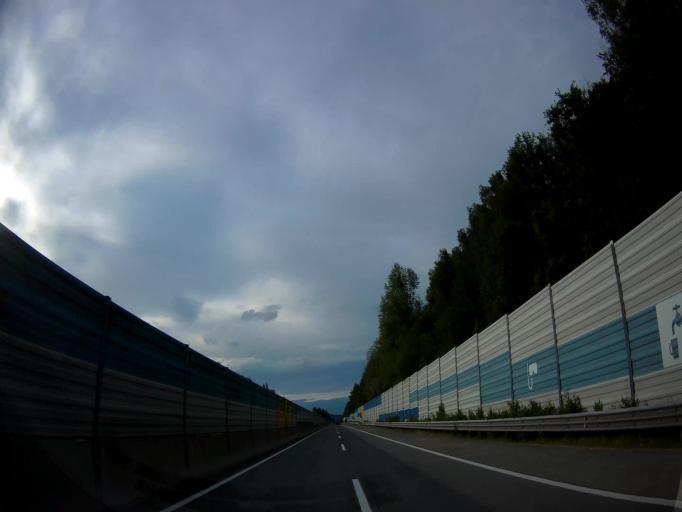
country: AT
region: Upper Austria
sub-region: Politischer Bezirk Vocklabruck
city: Oberwang
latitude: 47.8728
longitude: 13.4354
